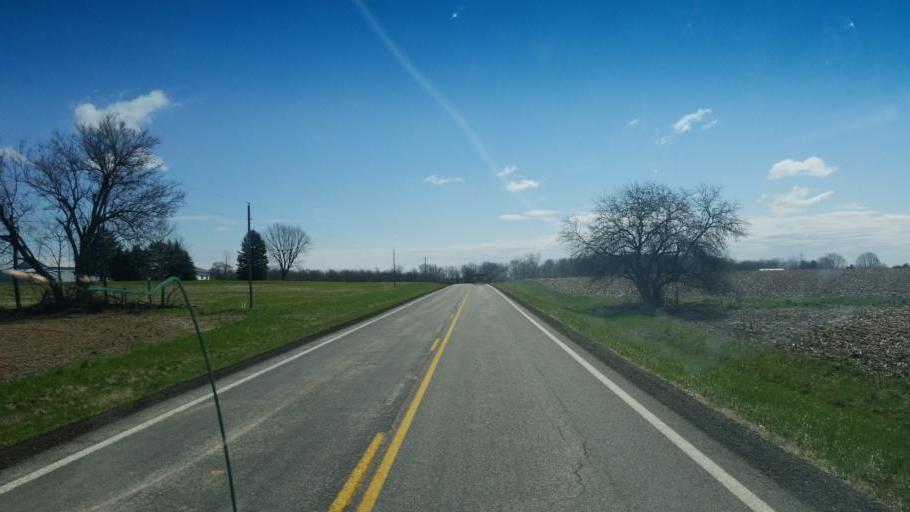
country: US
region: Ohio
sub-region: Crawford County
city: Crestline
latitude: 40.8576
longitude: -82.7925
